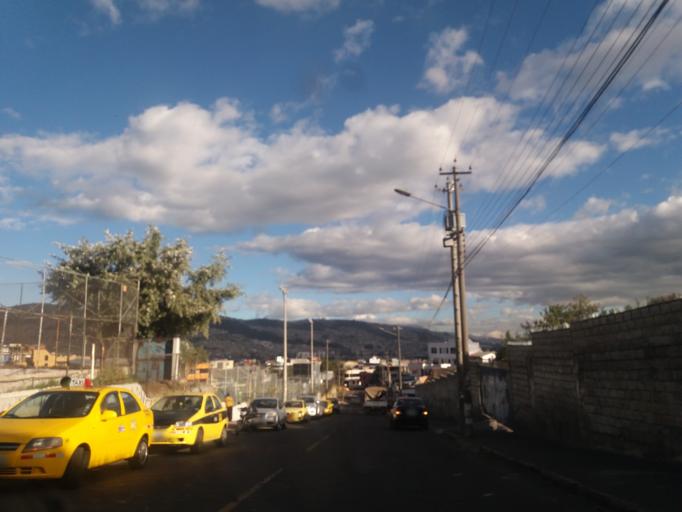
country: EC
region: Pichincha
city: Quito
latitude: -0.2344
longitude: -78.5305
